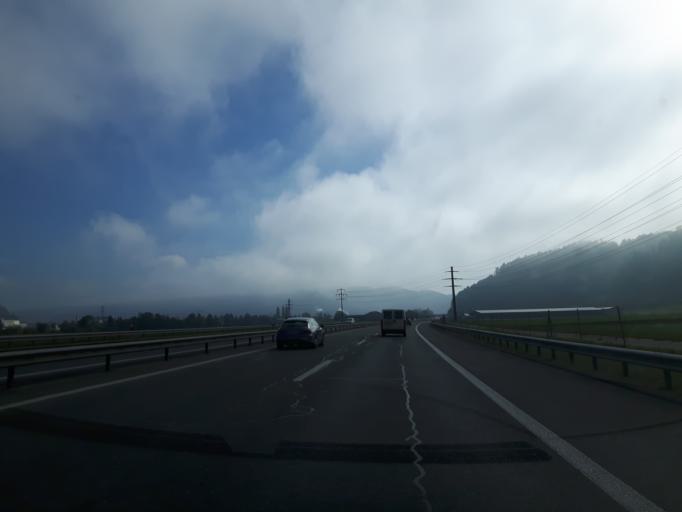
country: CH
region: Lucerne
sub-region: Willisau District
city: Dagmersellen
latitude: 47.2273
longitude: 7.9723
